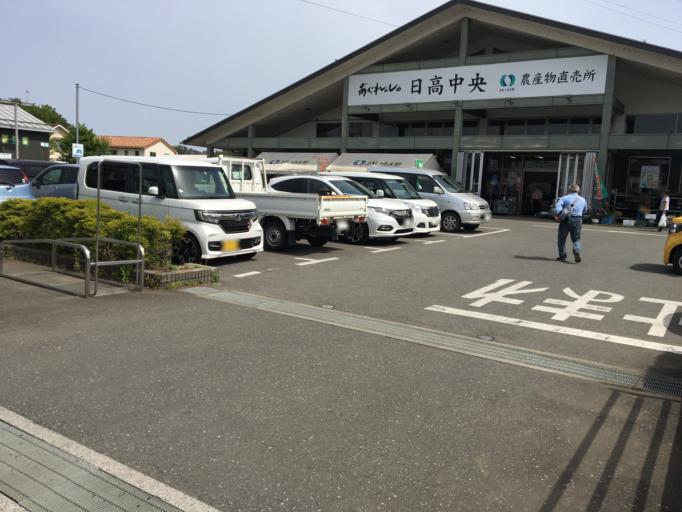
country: JP
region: Saitama
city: Hanno
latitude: 35.8897
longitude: 139.3313
